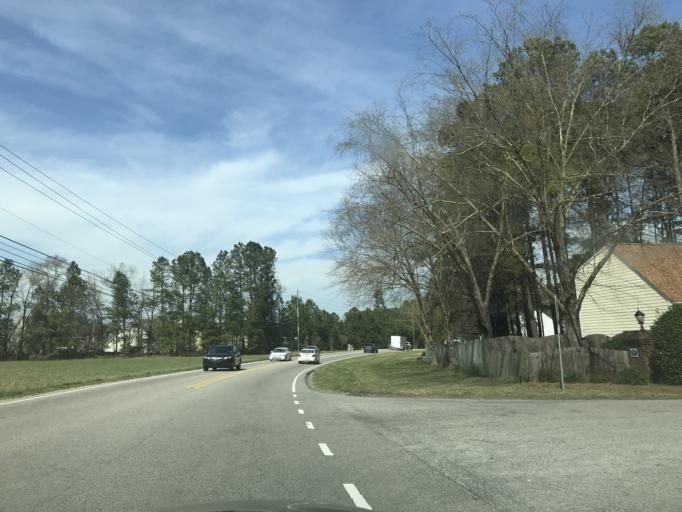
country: US
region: North Carolina
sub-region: Wake County
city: Knightdale
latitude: 35.8448
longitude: -78.5401
